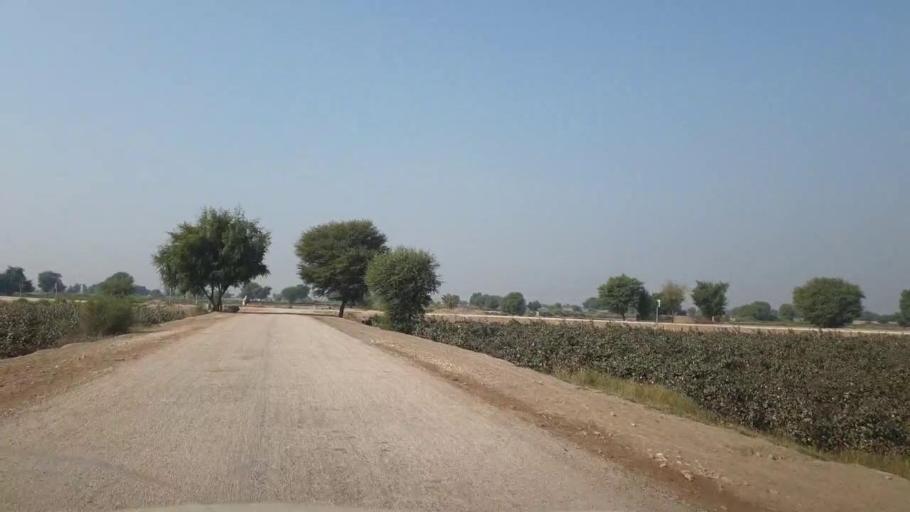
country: PK
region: Sindh
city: Bhan
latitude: 26.5070
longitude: 67.7850
